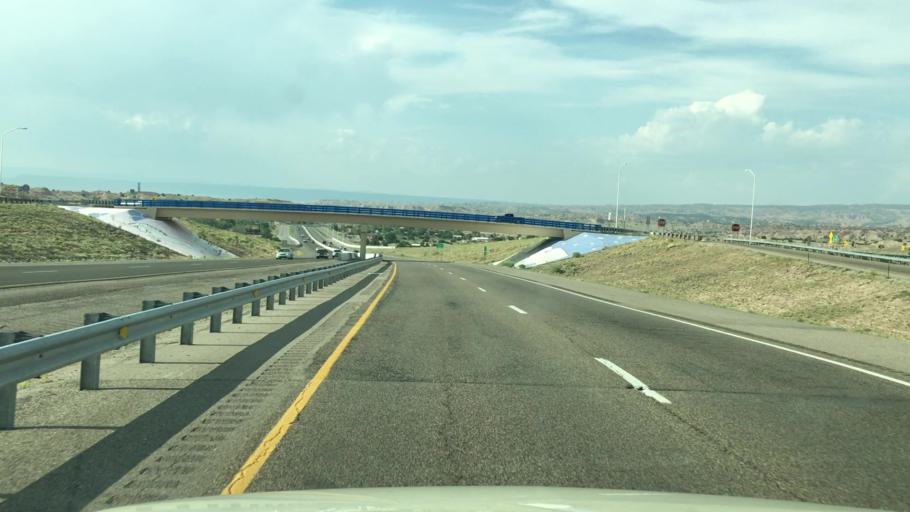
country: US
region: New Mexico
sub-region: Santa Fe County
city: Pojoaque
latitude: 35.9274
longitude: -106.0174
